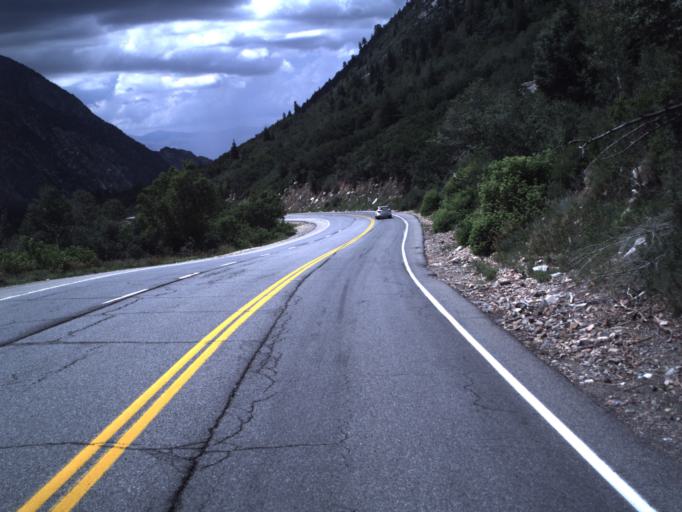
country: US
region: Utah
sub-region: Salt Lake County
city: Granite
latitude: 40.5744
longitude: -111.6927
